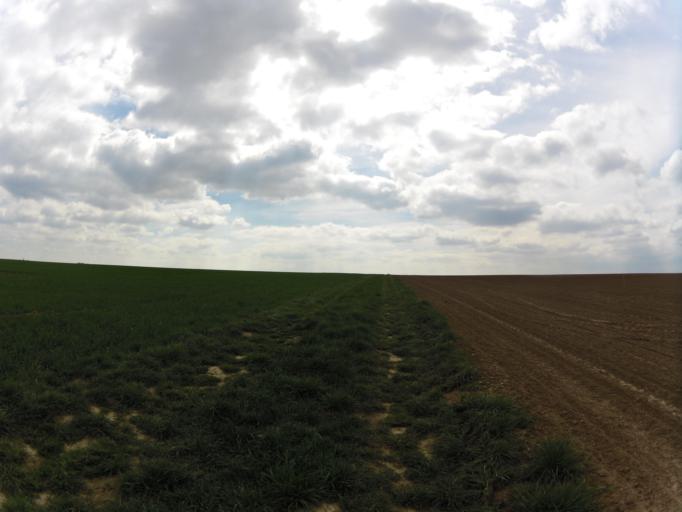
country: DE
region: Bavaria
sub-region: Regierungsbezirk Unterfranken
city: Giebelstadt
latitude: 49.6482
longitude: 9.9275
